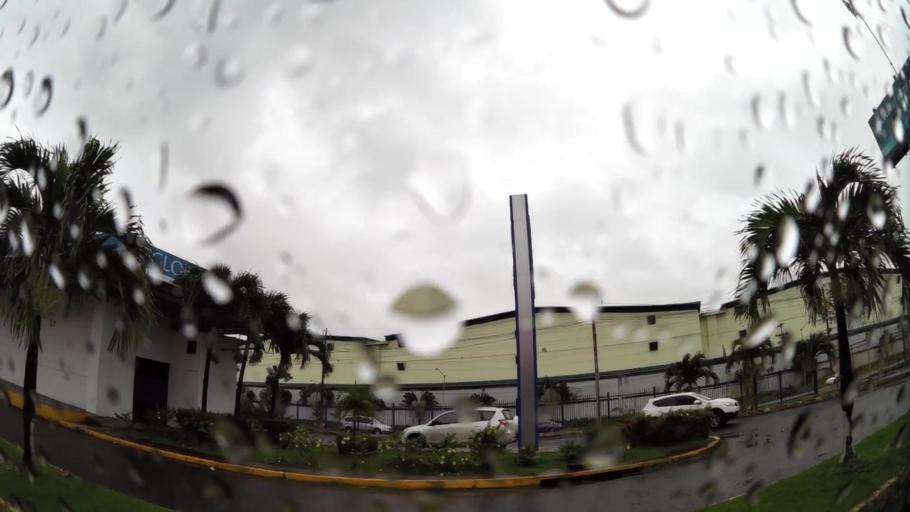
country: PA
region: Colon
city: Arco Iris
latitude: 9.3384
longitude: -79.8836
